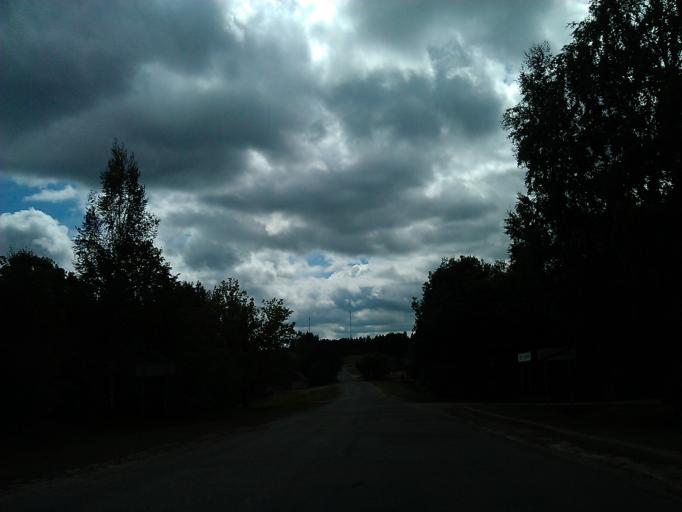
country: LV
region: Kuldigas Rajons
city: Kuldiga
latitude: 56.9621
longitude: 21.9497
